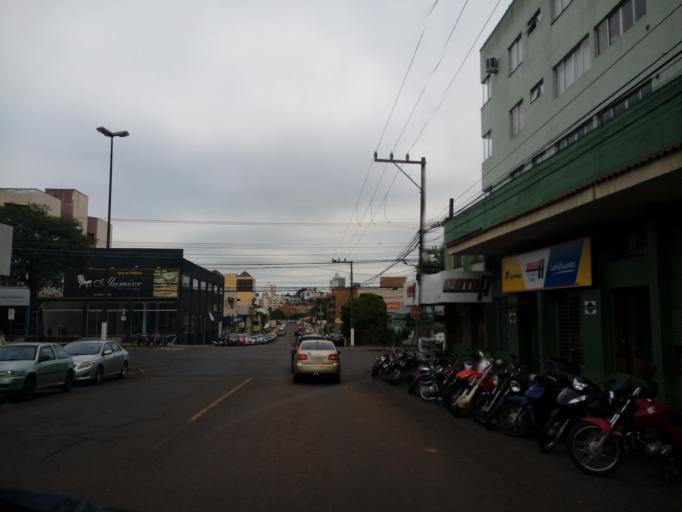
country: BR
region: Santa Catarina
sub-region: Chapeco
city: Chapeco
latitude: -27.0913
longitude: -52.6197
